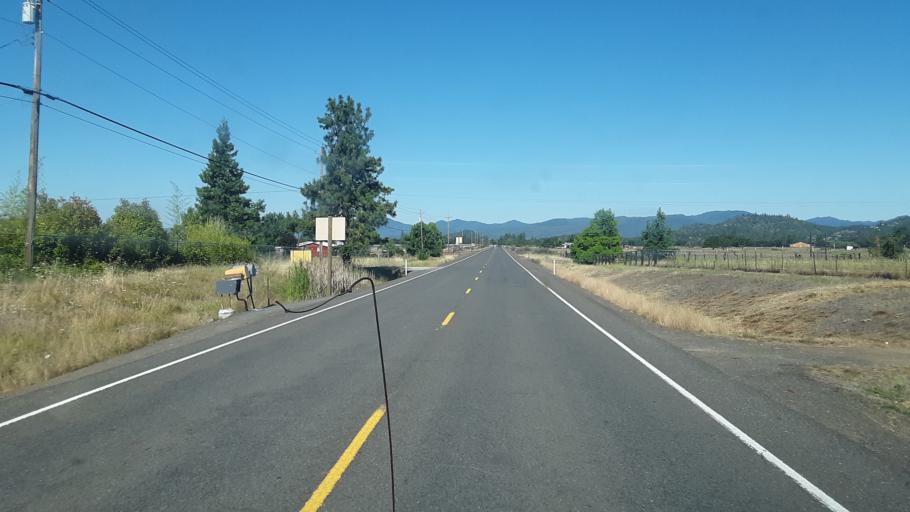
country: US
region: Oregon
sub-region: Jackson County
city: Eagle Point
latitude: 42.5236
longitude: -122.8181
